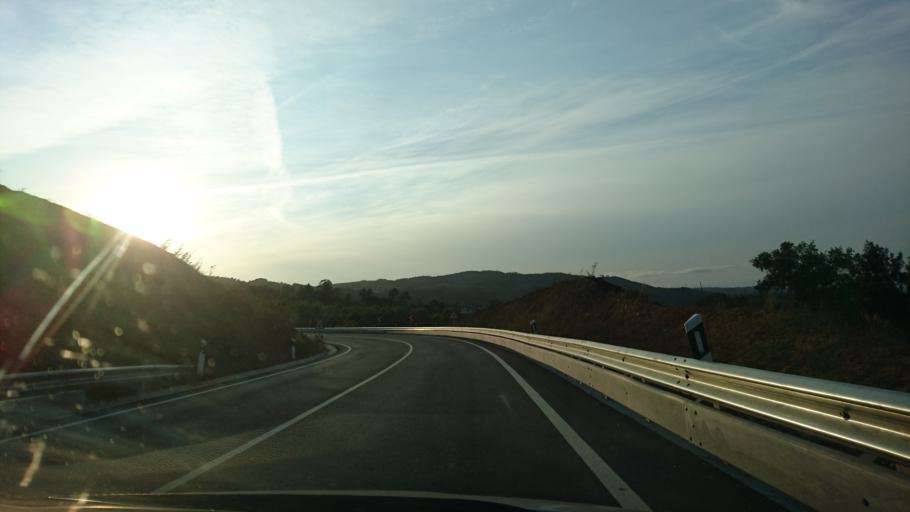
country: PT
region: Vila Real
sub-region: Mondim de Basto
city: Mondim de Basto
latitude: 41.4101
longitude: -7.9773
